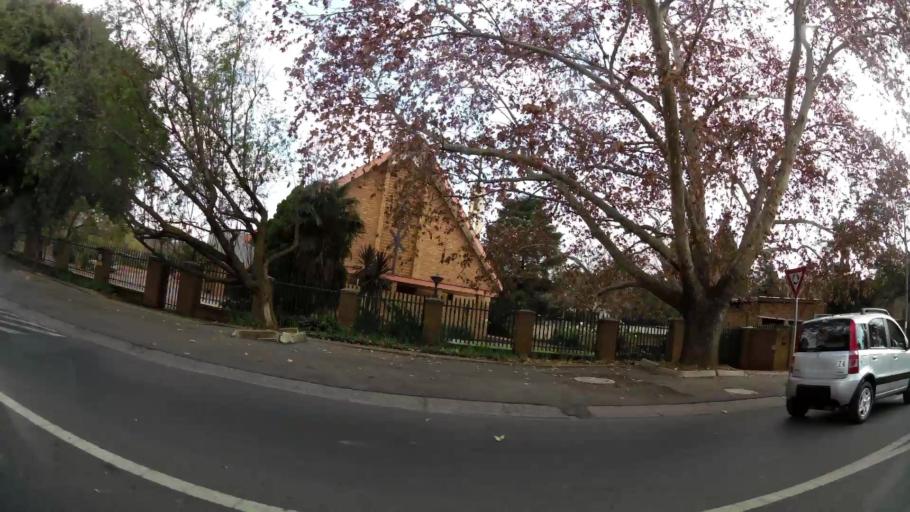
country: ZA
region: Gauteng
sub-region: City of Tshwane Metropolitan Municipality
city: Pretoria
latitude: -25.7751
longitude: 28.2824
